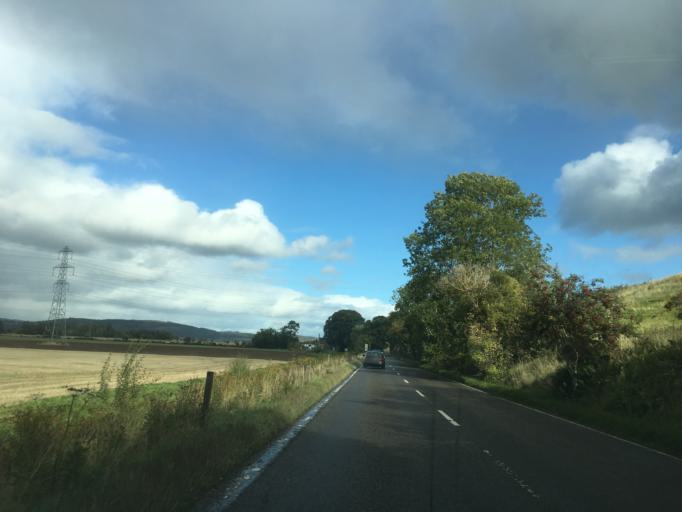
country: GB
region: Scotland
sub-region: Highland
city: Beauly
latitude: 57.4681
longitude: -4.3988
